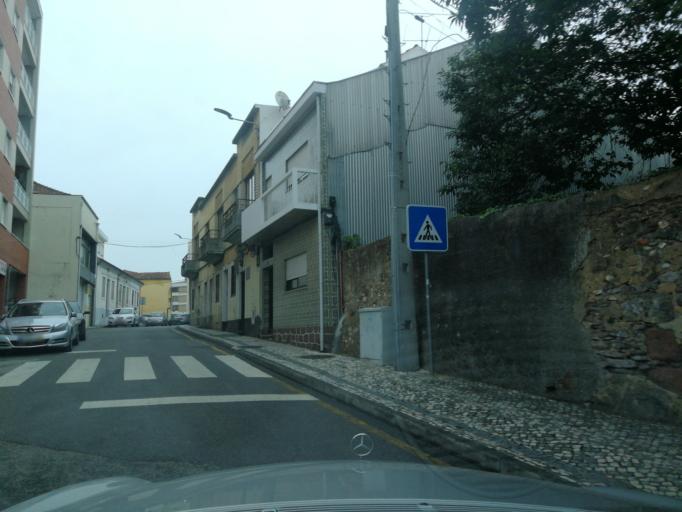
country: PT
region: Aveiro
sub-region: Agueda
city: Agueda
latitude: 40.5745
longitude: -8.4479
